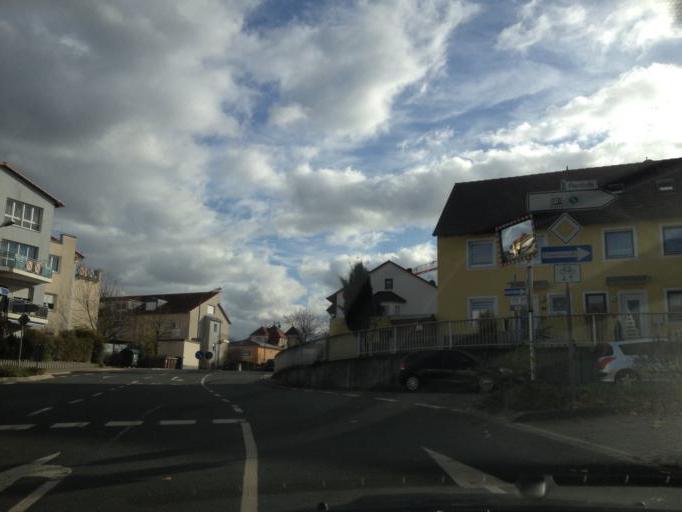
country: DE
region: Bavaria
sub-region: Regierungsbezirk Mittelfranken
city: Lauf an der Pegnitz
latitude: 49.5080
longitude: 11.2902
